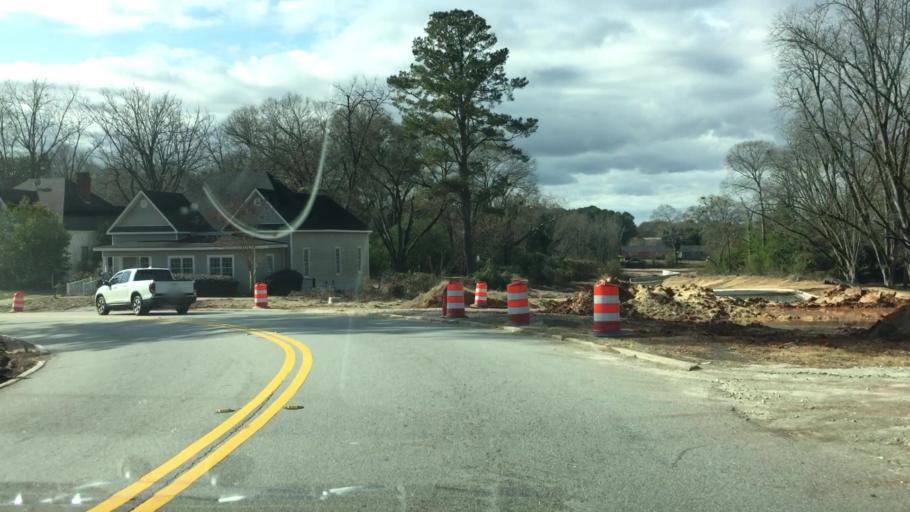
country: US
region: Georgia
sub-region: Henry County
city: McDonough
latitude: 33.4470
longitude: -84.1492
